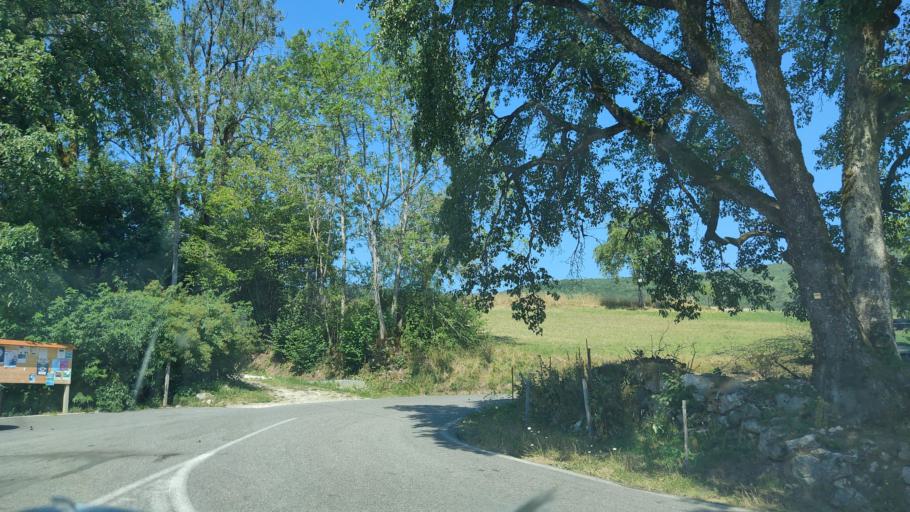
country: FR
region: Rhone-Alpes
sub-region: Departement de la Haute-Savoie
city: Gruffy
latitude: 45.7168
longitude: 6.0882
